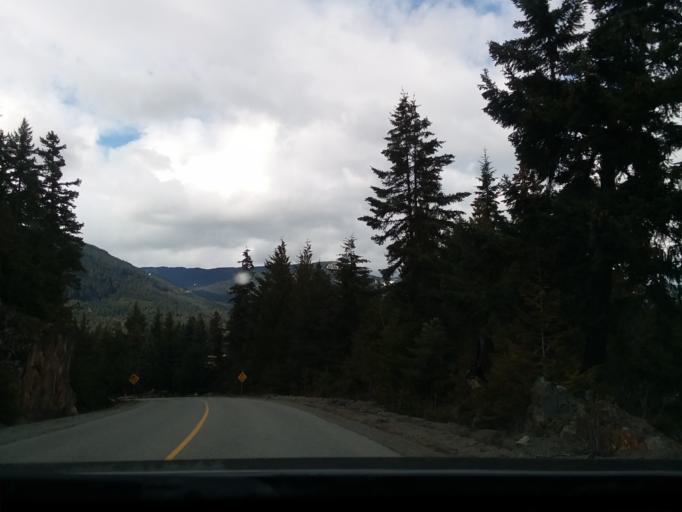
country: CA
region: British Columbia
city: Whistler
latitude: 50.1197
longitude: -122.9687
